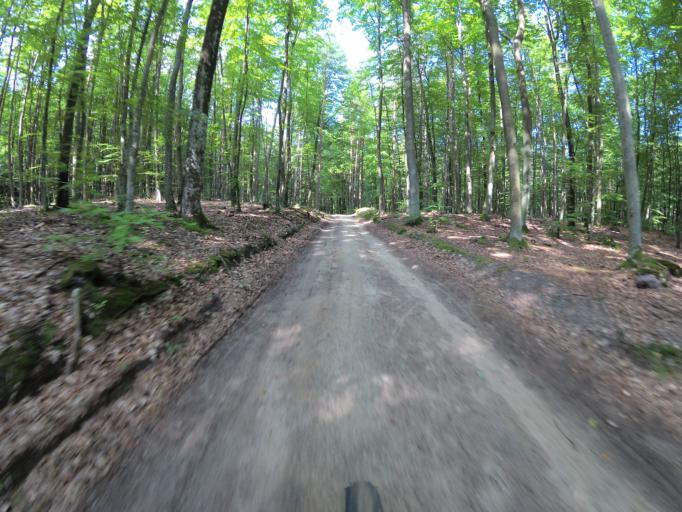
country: PL
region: Pomeranian Voivodeship
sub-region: Gdynia
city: Wielki Kack
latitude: 54.4962
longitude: 18.4799
